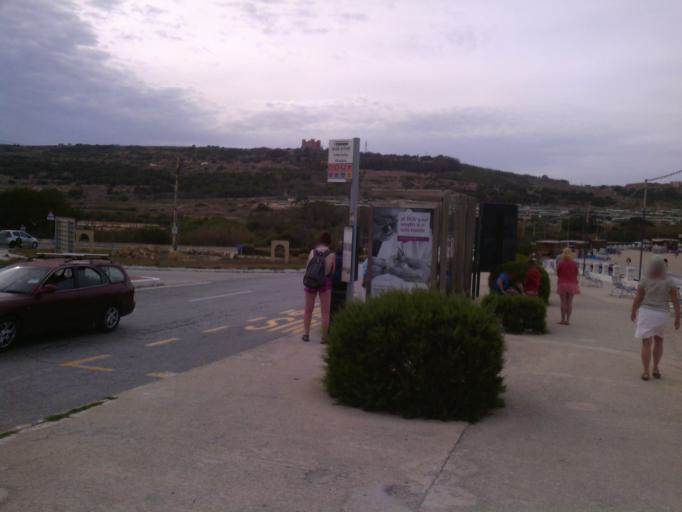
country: MT
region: Il-Mellieha
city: Mellieha
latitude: 35.9692
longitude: 14.3503
